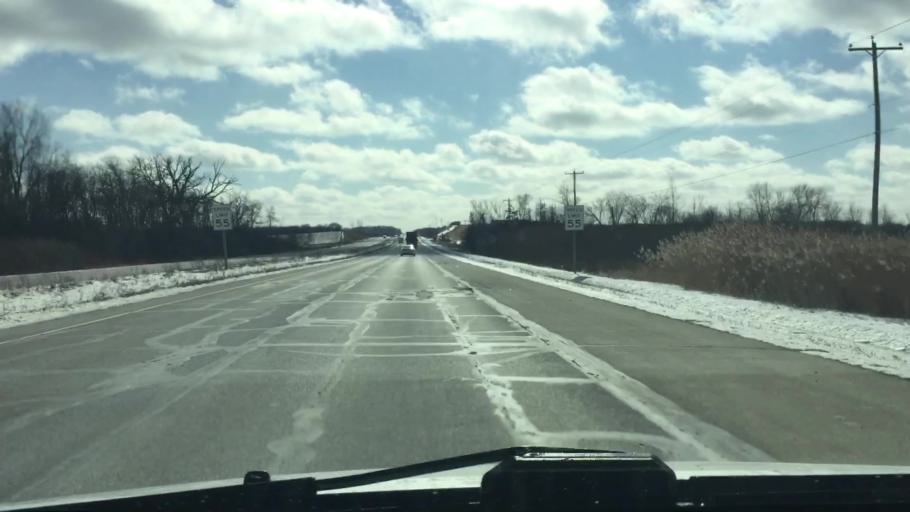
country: US
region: Wisconsin
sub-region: Waukesha County
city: Waukesha
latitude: 42.9690
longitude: -88.2278
